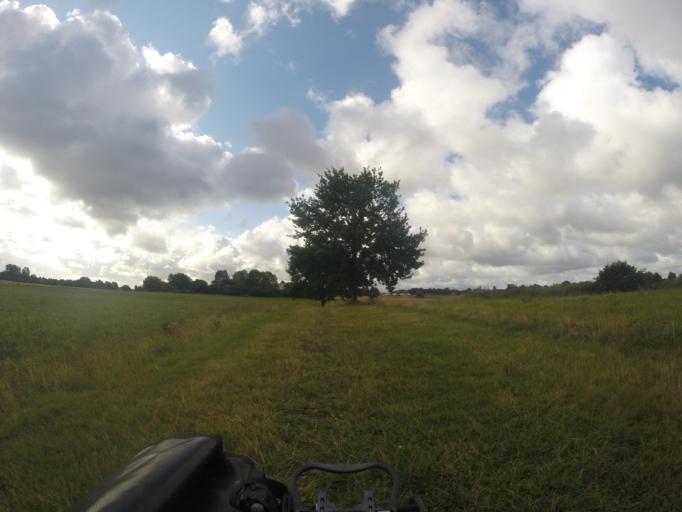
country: DK
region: Capital Region
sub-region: Herlev Kommune
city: Herlev
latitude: 55.7493
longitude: 12.4316
